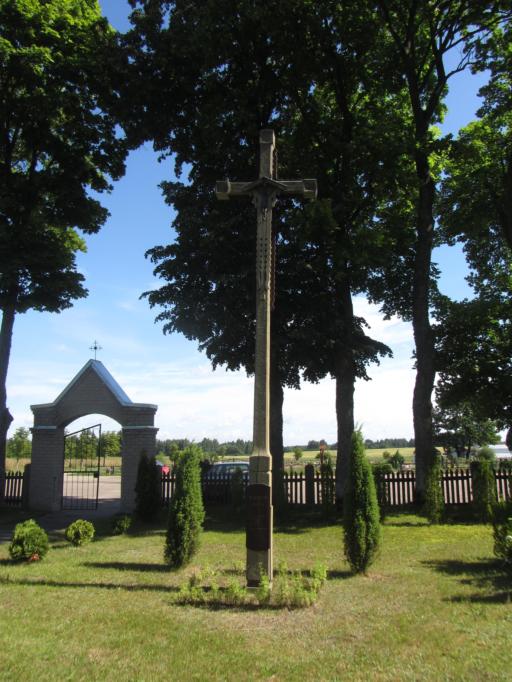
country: LT
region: Vilnius County
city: Elektrenai
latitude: 54.9113
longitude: 24.7225
